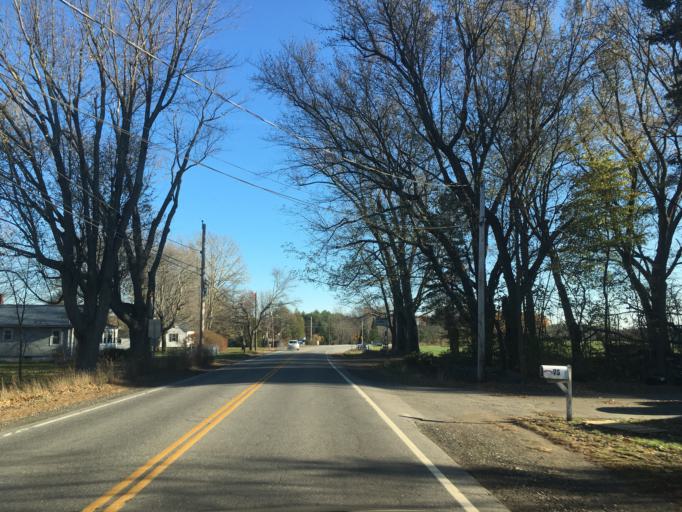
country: US
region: New Hampshire
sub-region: Rockingham County
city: Stratham Station
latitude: 43.0378
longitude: -70.9248
